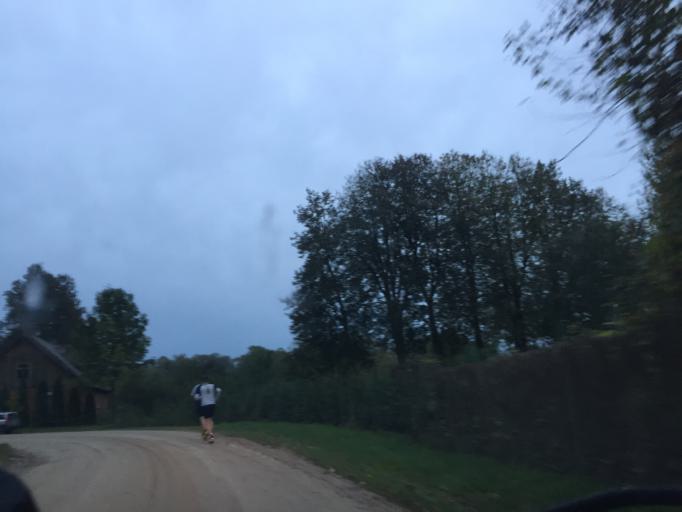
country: LV
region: Adazi
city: Adazi
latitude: 57.0843
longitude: 24.3503
